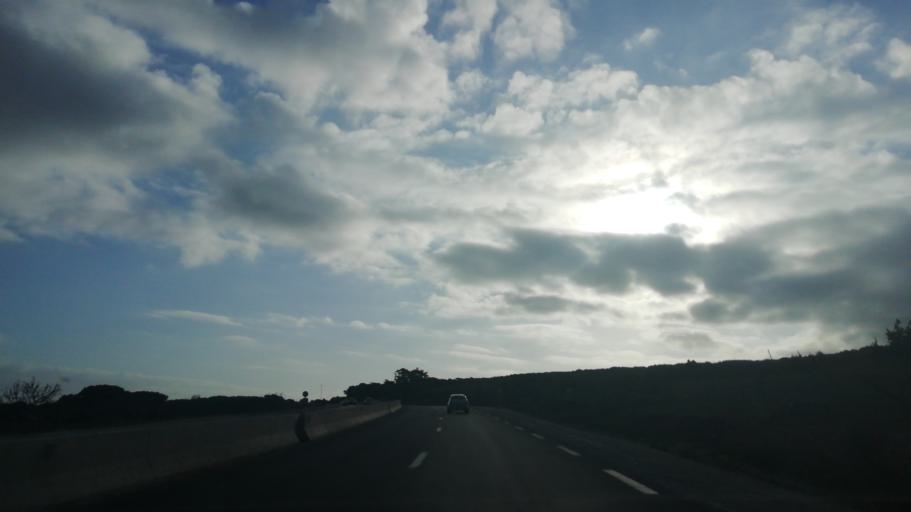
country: DZ
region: Mostaganem
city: Mostaganem
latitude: 36.1124
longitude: 0.2470
